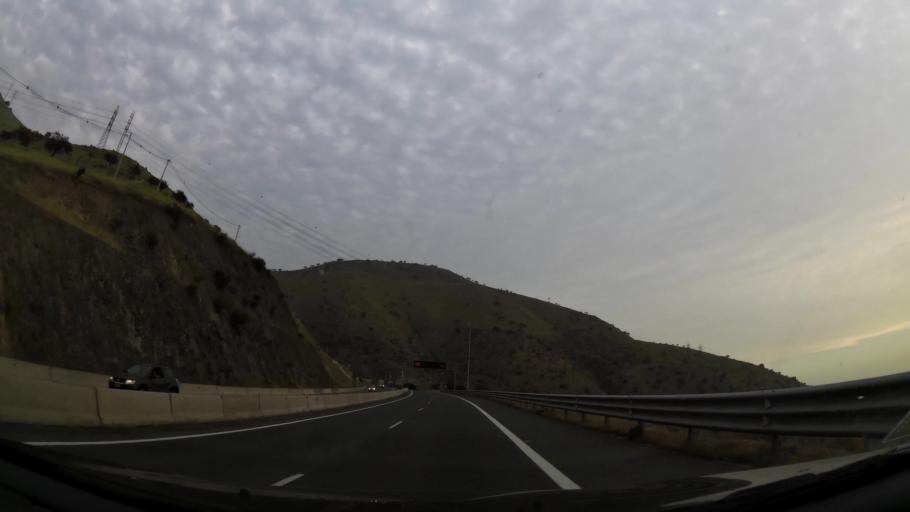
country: CL
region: Santiago Metropolitan
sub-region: Provincia de Chacabuco
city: Chicureo Abajo
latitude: -33.3628
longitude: -70.6179
